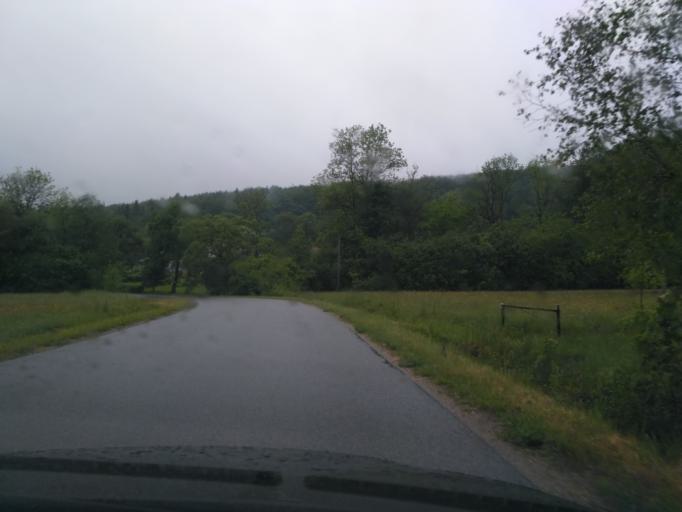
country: PL
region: Lesser Poland Voivodeship
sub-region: Powiat gorlicki
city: Kobylanka
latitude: 49.6274
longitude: 21.2523
